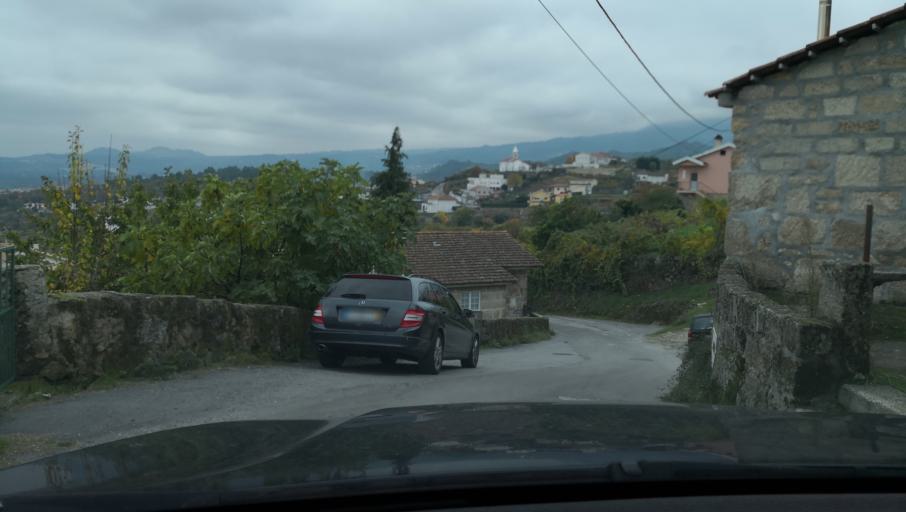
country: PT
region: Vila Real
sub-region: Vila Real
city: Vila Real
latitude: 41.3221
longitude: -7.7624
